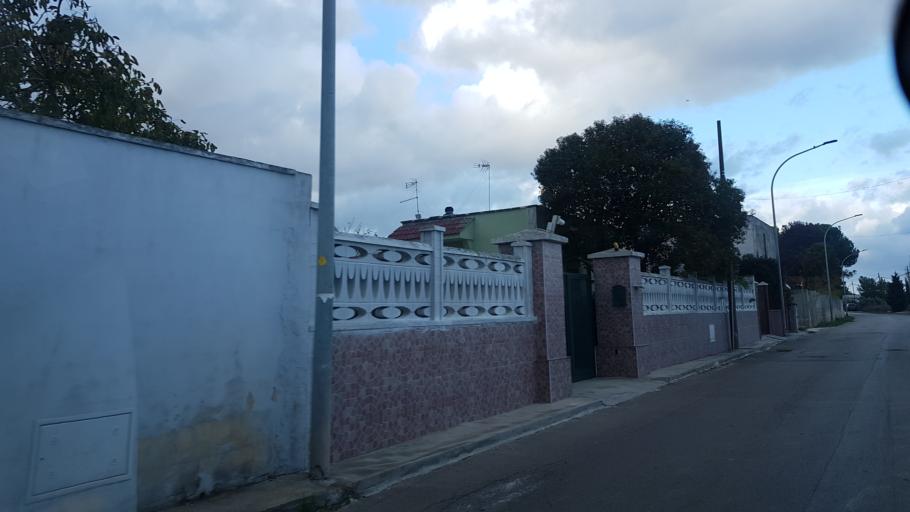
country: IT
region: Apulia
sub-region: Provincia di Brindisi
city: San Pietro Vernotico
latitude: 40.4928
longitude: 18.0006
